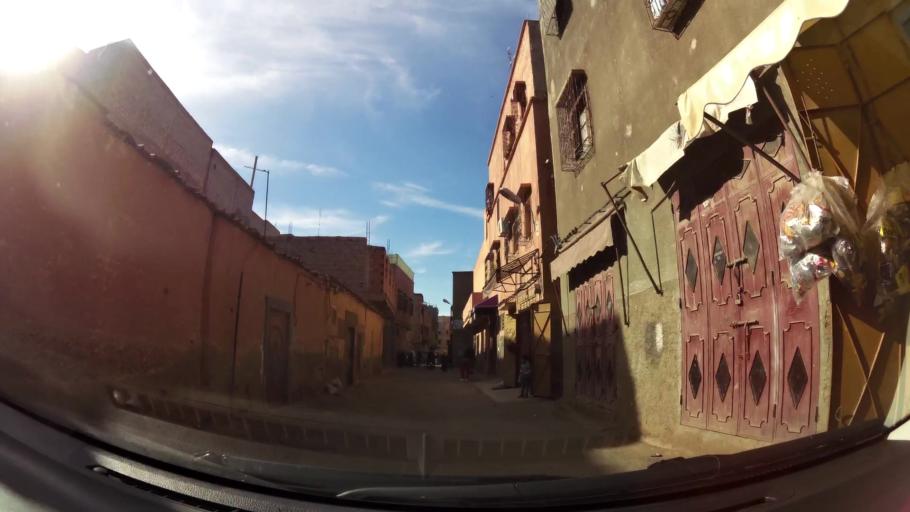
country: MA
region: Marrakech-Tensift-Al Haouz
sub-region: Marrakech
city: Marrakesh
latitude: 31.6142
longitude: -7.9659
